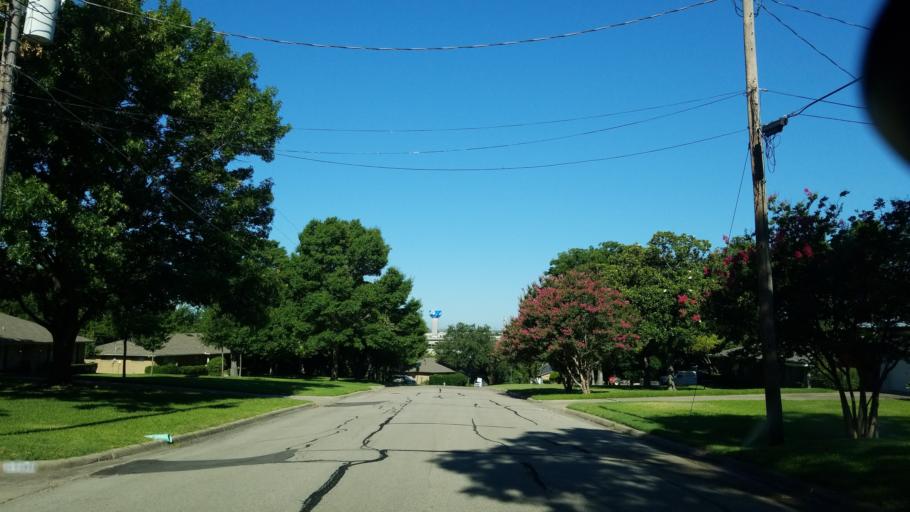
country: US
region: Texas
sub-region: Dallas County
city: Carrollton
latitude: 32.9506
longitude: -96.9012
